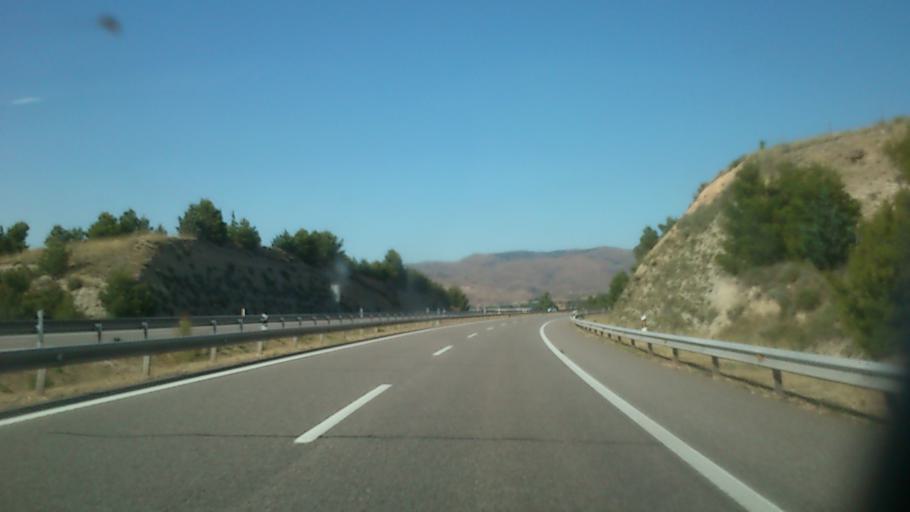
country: ES
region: Aragon
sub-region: Provincia de Zaragoza
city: Calatayud
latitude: 41.3450
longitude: -1.6293
